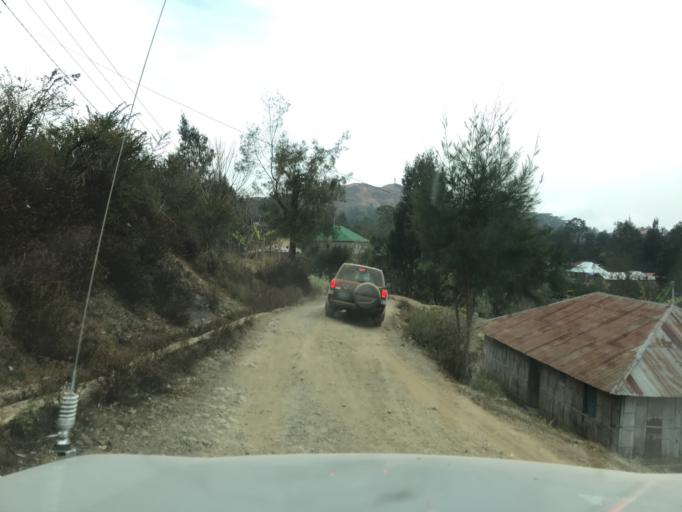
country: TL
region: Ermera
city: Gleno
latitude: -8.8293
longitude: 125.4530
